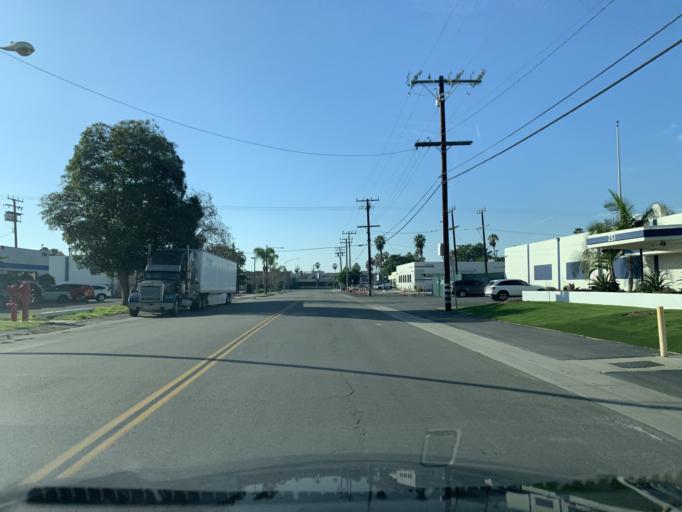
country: US
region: California
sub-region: Orange County
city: Anaheim
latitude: 33.8136
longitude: -117.9045
